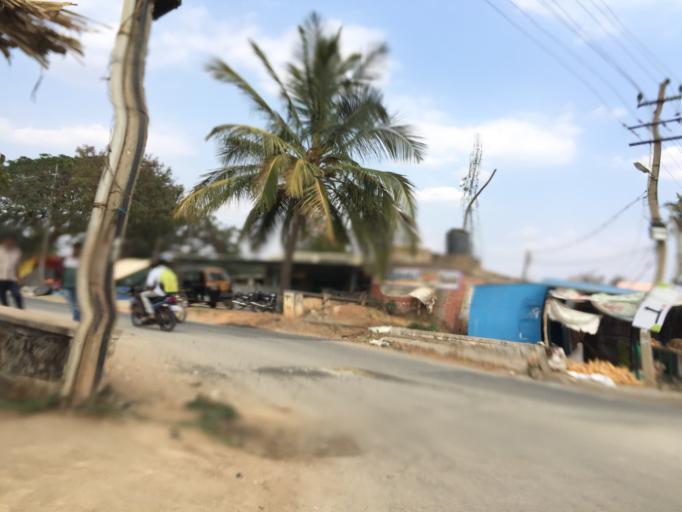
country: IN
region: Karnataka
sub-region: Chikkaballapur
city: Chik Ballapur
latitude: 13.3875
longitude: 77.6987
